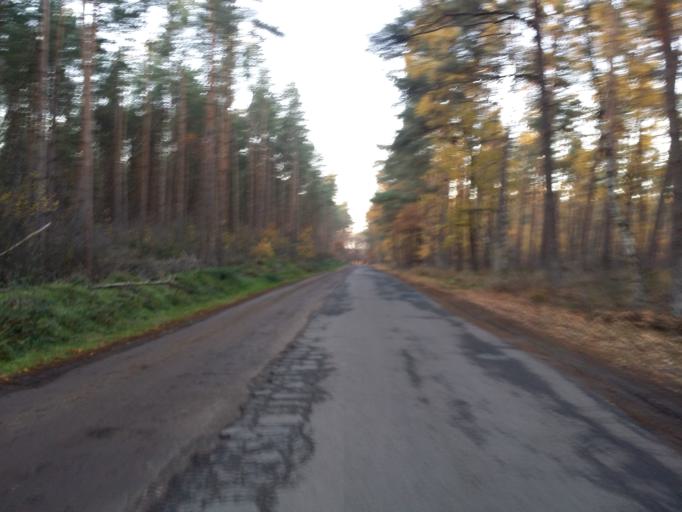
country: DE
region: Lower Saxony
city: Ahausen
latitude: 53.0798
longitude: 9.3052
